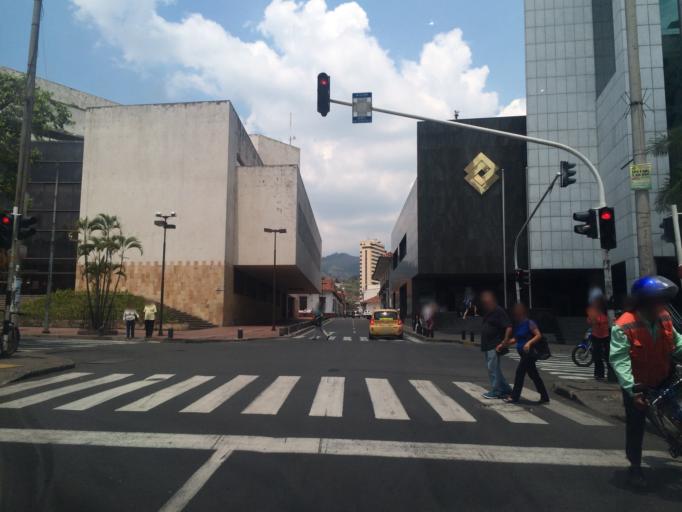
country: CO
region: Valle del Cauca
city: Cali
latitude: 3.4510
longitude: -76.5351
